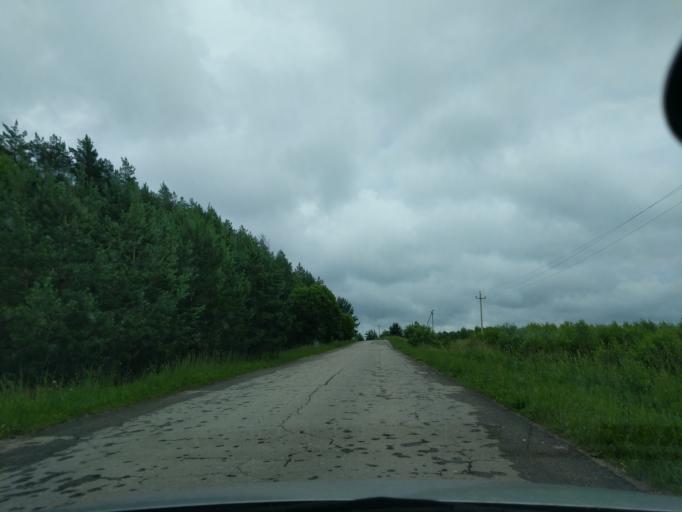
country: RU
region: Kaluga
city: Myatlevo
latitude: 54.8294
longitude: 35.6526
